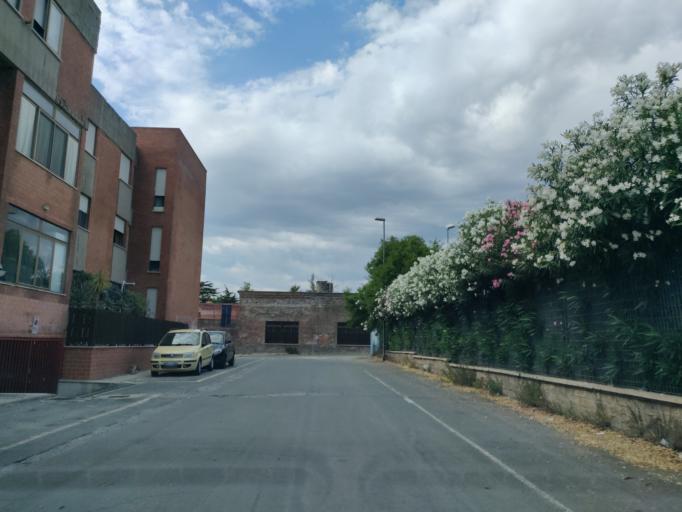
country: IT
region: Latium
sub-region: Citta metropolitana di Roma Capitale
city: Civitavecchia
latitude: 42.0872
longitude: 11.8101
